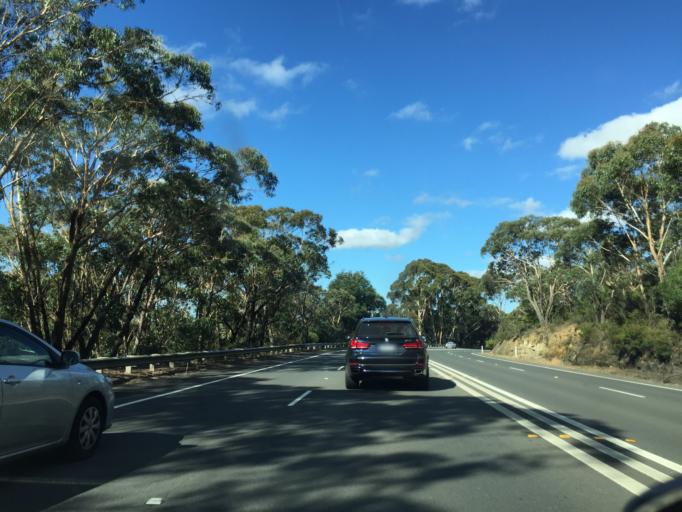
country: AU
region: New South Wales
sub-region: Blue Mountains Municipality
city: Leura
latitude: -33.7086
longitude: 150.3447
